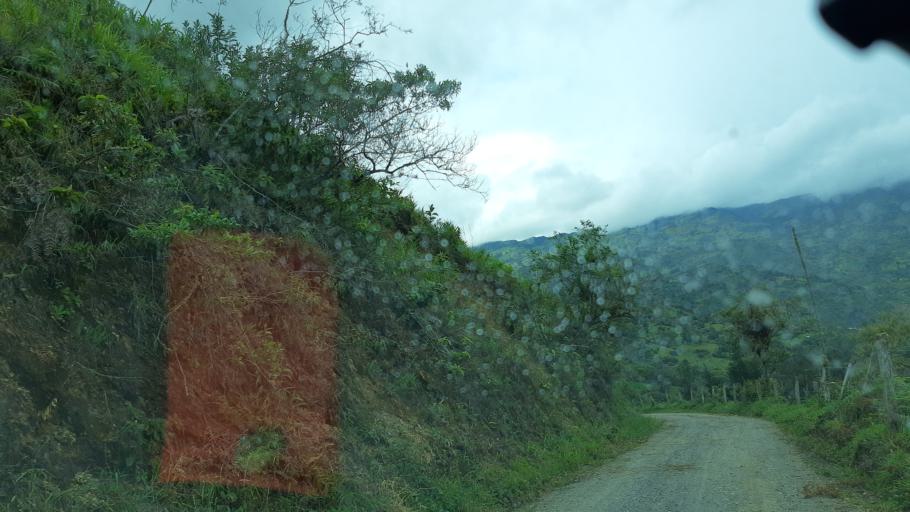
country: CO
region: Boyaca
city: Garagoa
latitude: 5.0380
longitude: -73.3594
